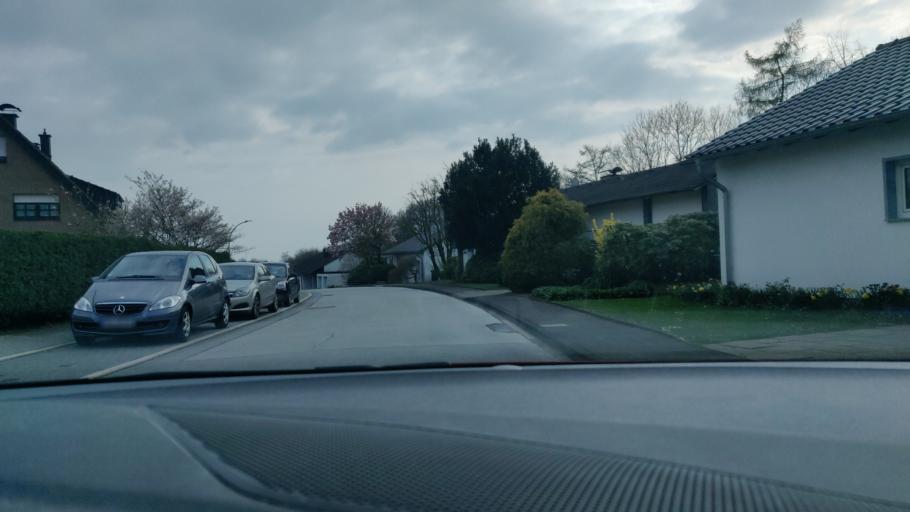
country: DE
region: North Rhine-Westphalia
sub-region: Regierungsbezirk Dusseldorf
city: Velbert
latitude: 51.3269
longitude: 7.0209
